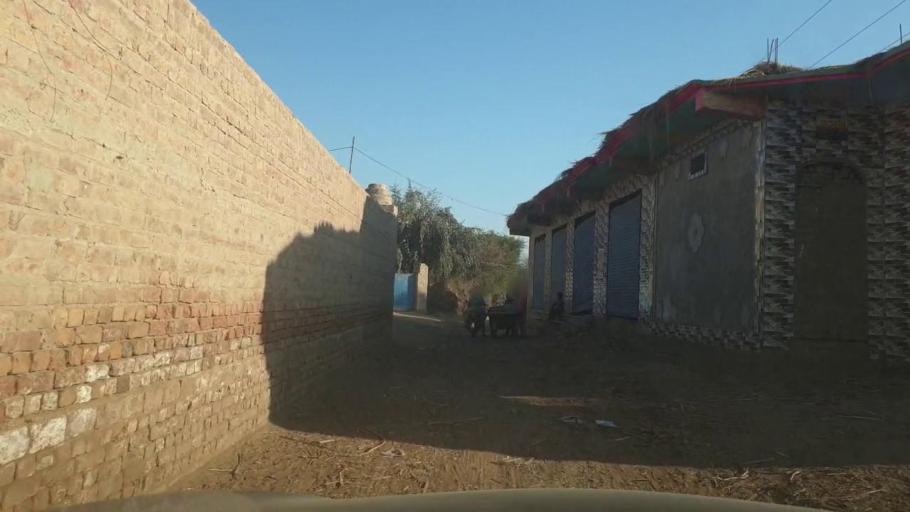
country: PK
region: Sindh
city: Ghotki
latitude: 28.0669
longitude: 69.3692
